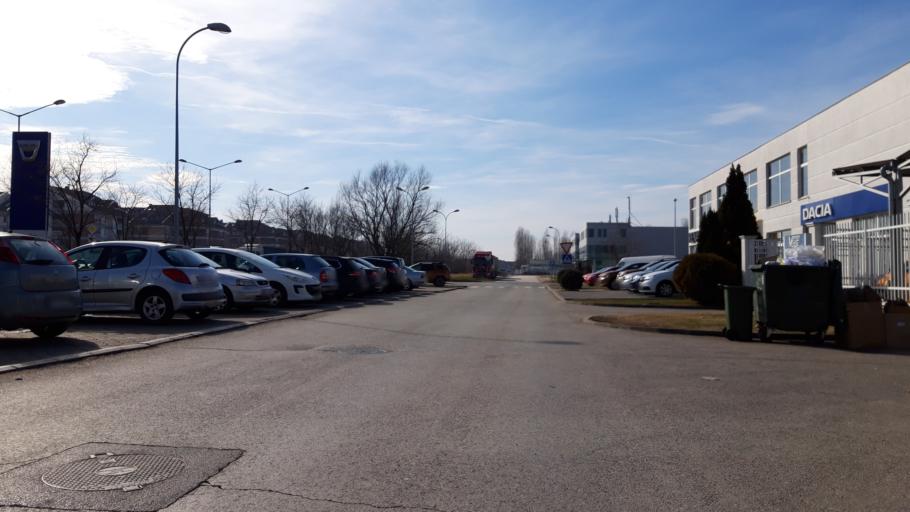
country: RS
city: Veternik
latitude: 45.2542
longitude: 19.7899
